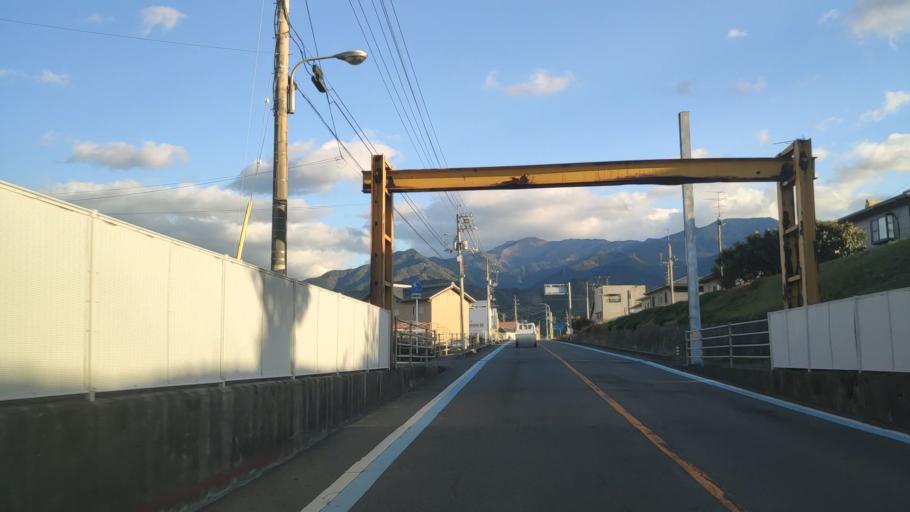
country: JP
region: Ehime
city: Saijo
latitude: 33.9091
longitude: 133.1826
